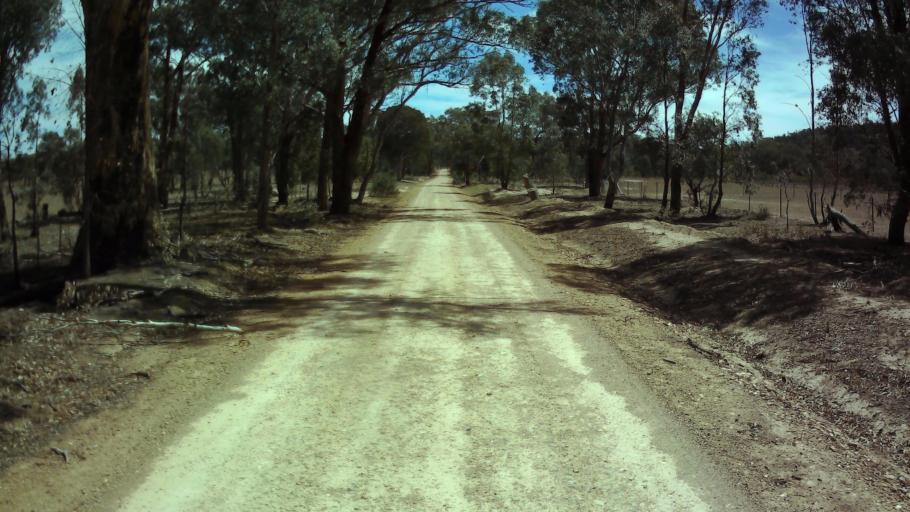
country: AU
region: New South Wales
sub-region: Weddin
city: Grenfell
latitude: -33.7471
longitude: 148.1957
